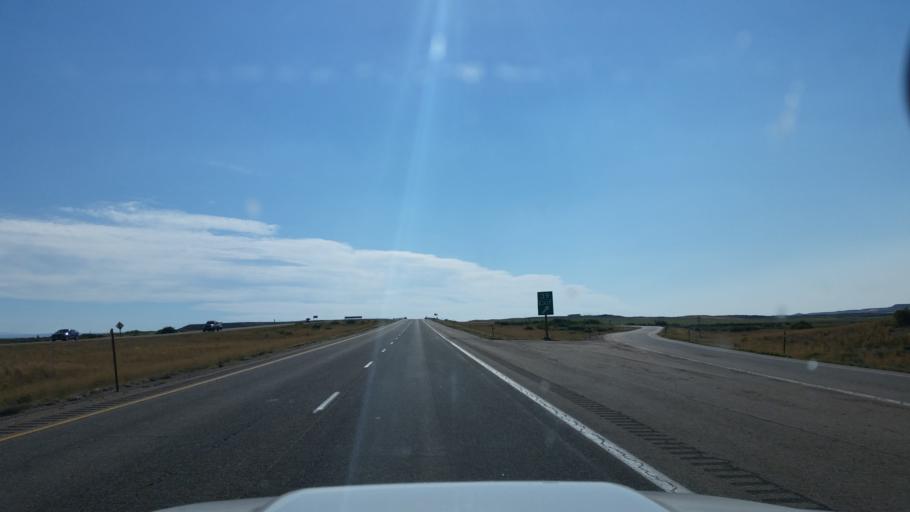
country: US
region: Wyoming
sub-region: Uinta County
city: Lyman
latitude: 41.3587
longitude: -110.3329
